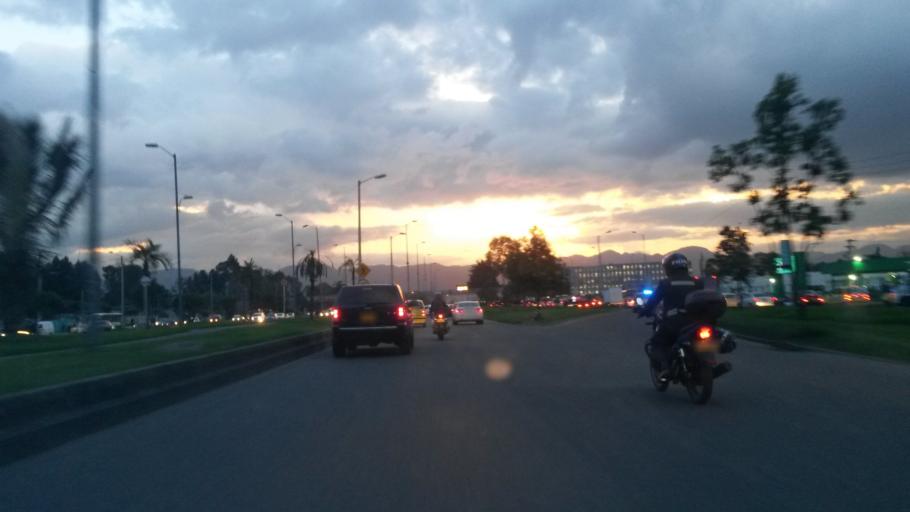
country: CO
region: Bogota D.C.
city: Bogota
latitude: 4.6861
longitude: -74.1266
